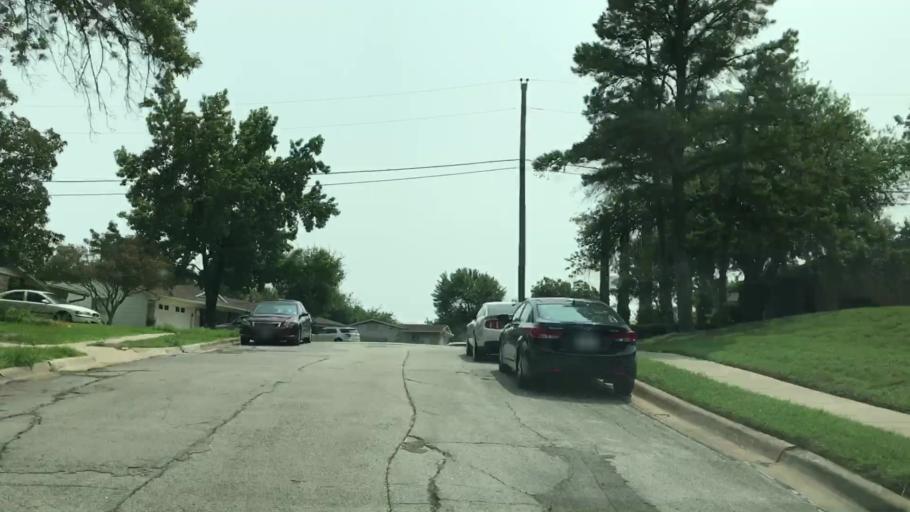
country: US
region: Texas
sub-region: Dallas County
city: Irving
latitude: 32.8410
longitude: -97.0013
